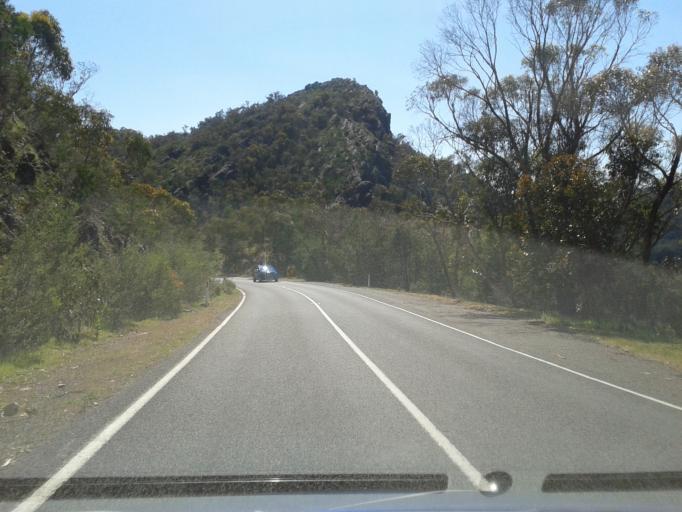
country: AU
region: Victoria
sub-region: Northern Grampians
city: Stawell
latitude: -37.1378
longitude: 142.5088
